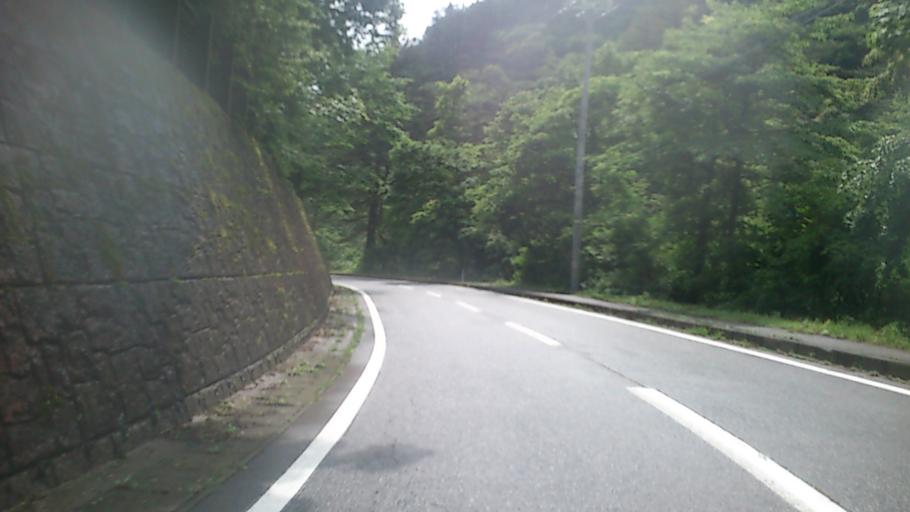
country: JP
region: Akita
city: Noshiromachi
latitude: 40.5524
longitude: 139.9482
